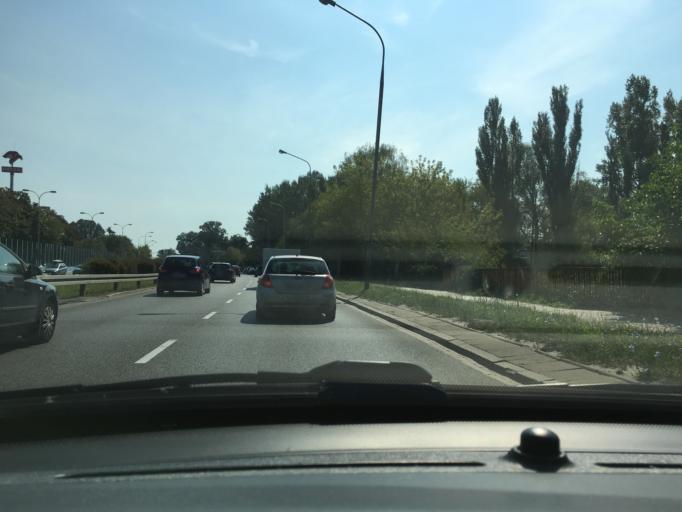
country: PL
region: Masovian Voivodeship
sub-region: Warszawa
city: Praga Poludnie
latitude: 52.2242
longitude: 21.0572
